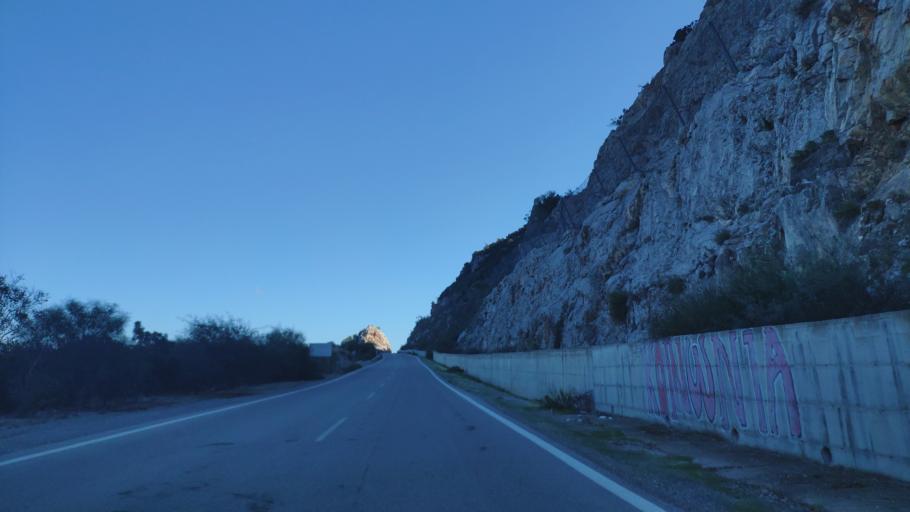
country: GR
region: Peloponnese
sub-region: Nomos Argolidos
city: Palaia Epidavros
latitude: 37.5863
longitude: 23.2227
